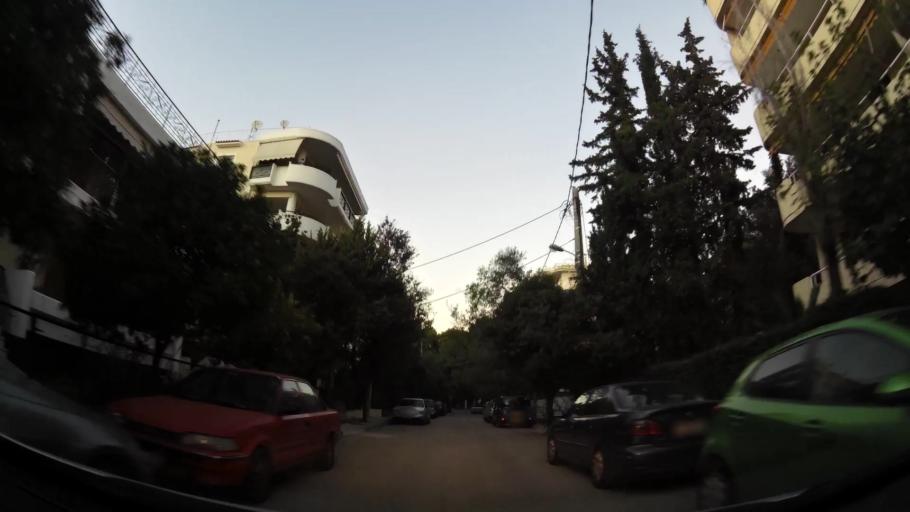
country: GR
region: Attica
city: Pefki
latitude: 38.0615
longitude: 23.7971
